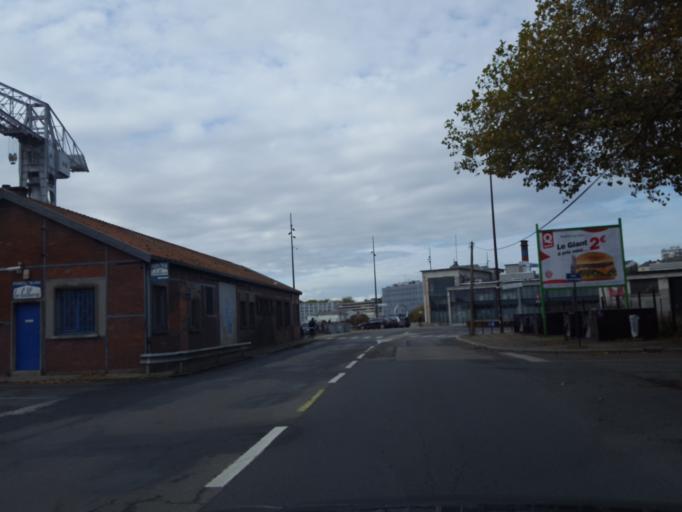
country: FR
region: Pays de la Loire
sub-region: Departement de la Loire-Atlantique
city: Nantes
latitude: 47.1999
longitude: -1.5724
